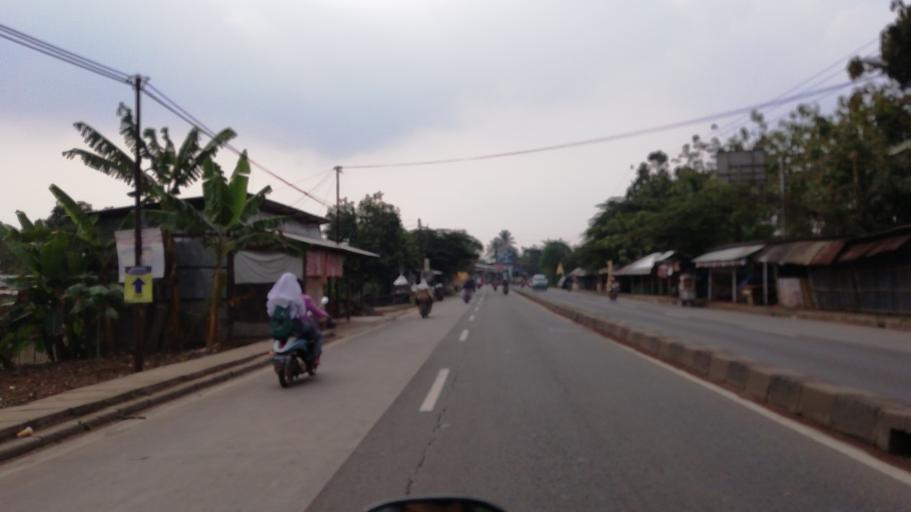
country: ID
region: West Java
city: Parung
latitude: -6.4845
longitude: 106.7345
